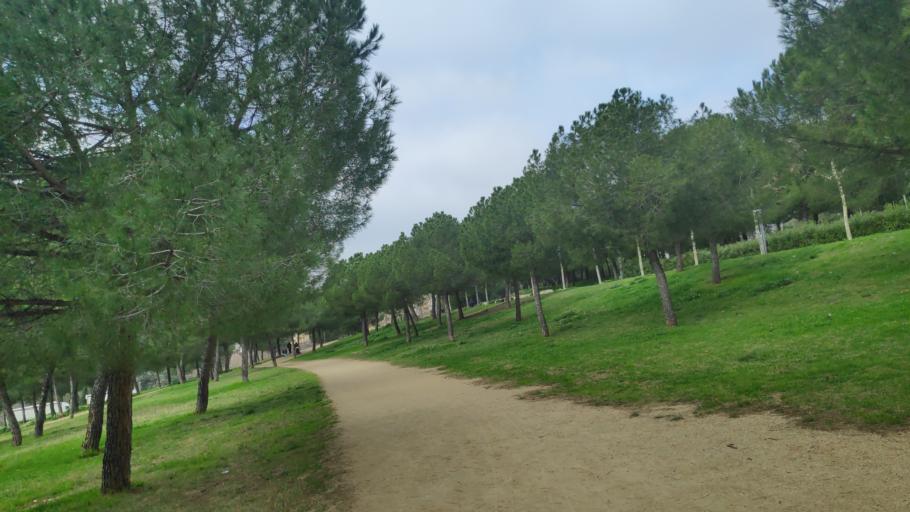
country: ES
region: Catalonia
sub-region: Provincia de Barcelona
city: Sant Quirze del Valles
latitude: 41.5516
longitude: 2.0912
